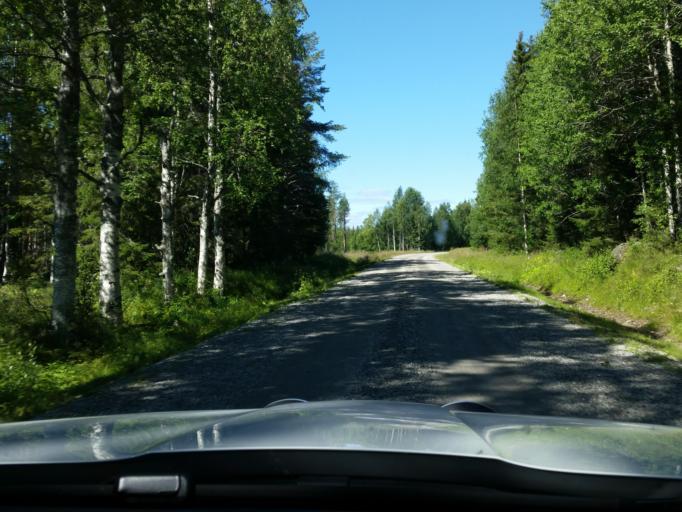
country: SE
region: Vaesterbotten
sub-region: Skelleftea Kommun
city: Storvik
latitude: 65.3069
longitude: 20.6369
